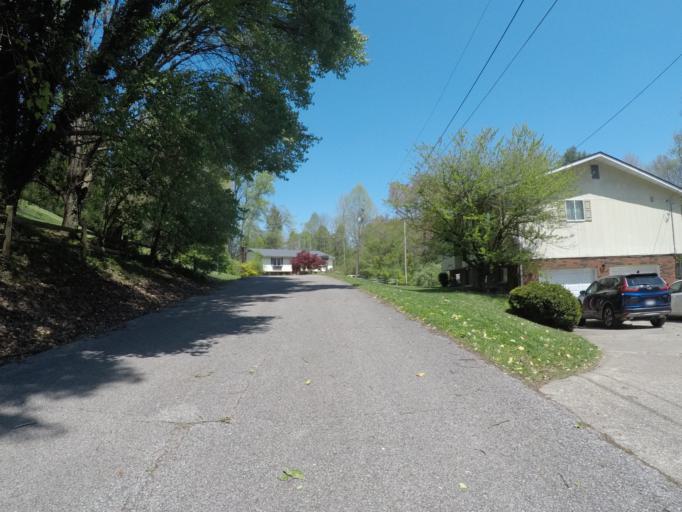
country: US
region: West Virginia
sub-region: Cabell County
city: Pea Ridge
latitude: 38.4084
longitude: -82.3401
